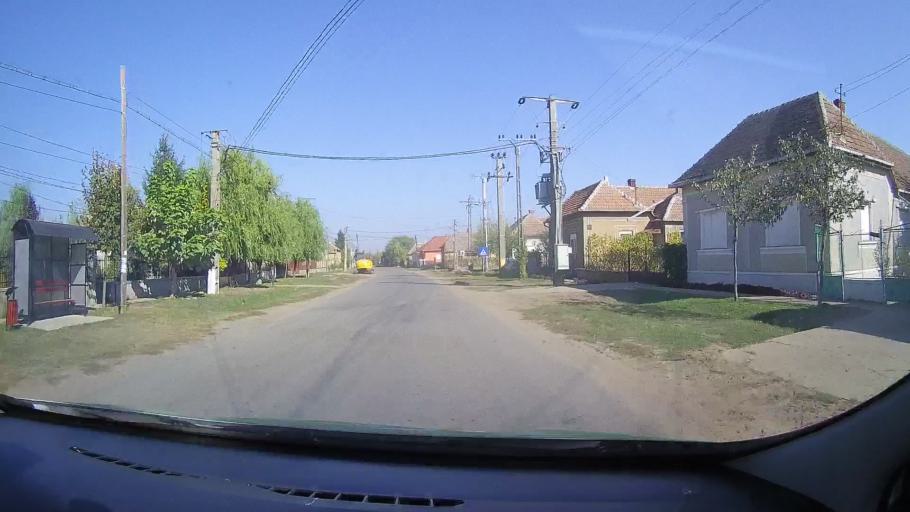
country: RO
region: Satu Mare
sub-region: Comuna Ciumesti
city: Ciumesti
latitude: 47.6632
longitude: 22.3363
